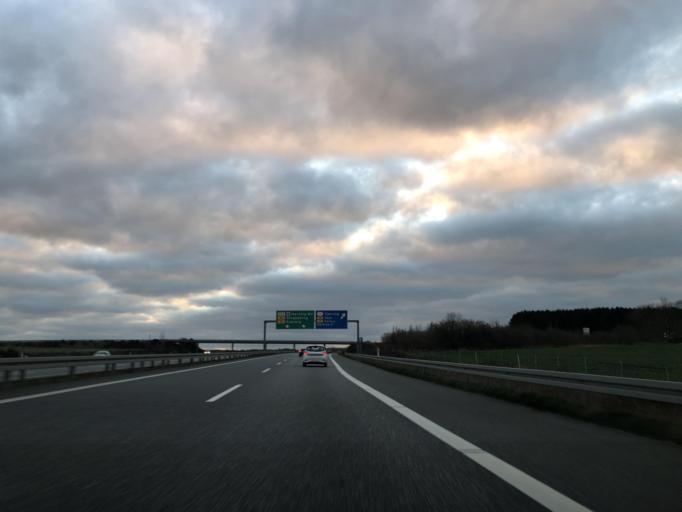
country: DK
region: Central Jutland
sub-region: Herning Kommune
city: Snejbjerg
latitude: 56.1995
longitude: 8.8782
